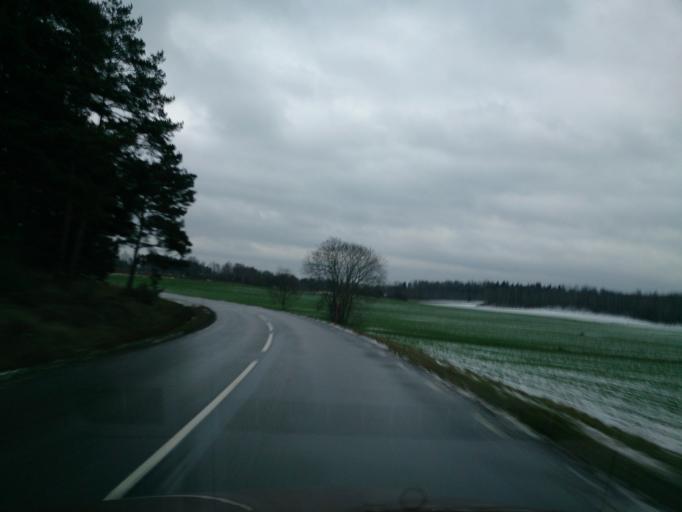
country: SE
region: OEstergoetland
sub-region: Norrkopings Kommun
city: Kimstad
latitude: 58.3966
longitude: 15.9562
